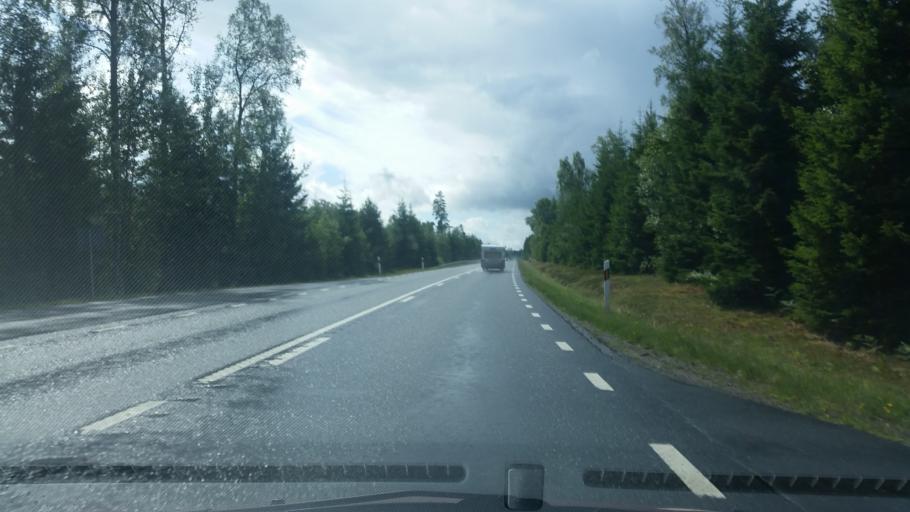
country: SE
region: Joenkoeping
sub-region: Gislaveds Kommun
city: Gislaved
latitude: 57.3726
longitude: 13.5763
